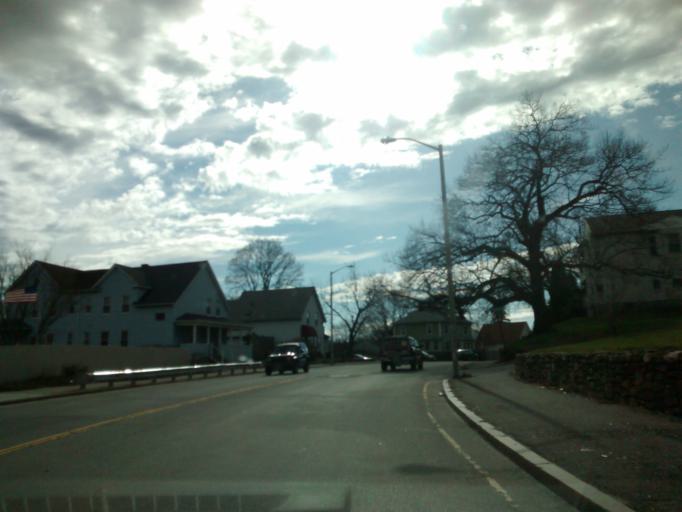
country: US
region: Massachusetts
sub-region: Worcester County
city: Sunderland
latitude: 42.2503
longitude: -71.7741
